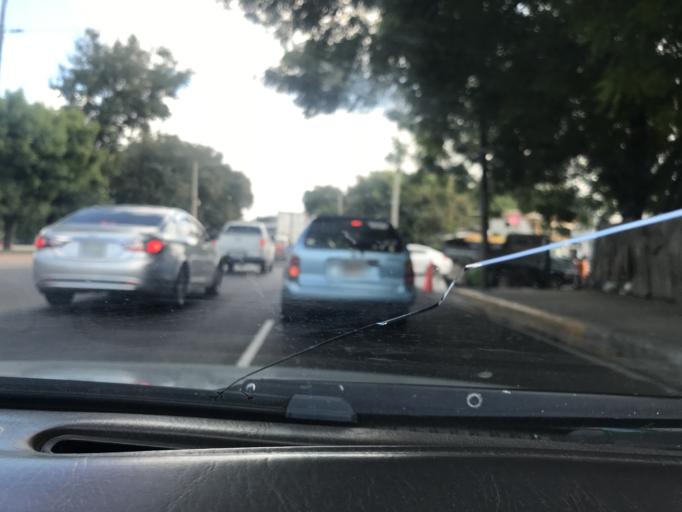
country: DO
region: Santiago
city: Santiago de los Caballeros
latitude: 19.4698
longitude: -70.7162
